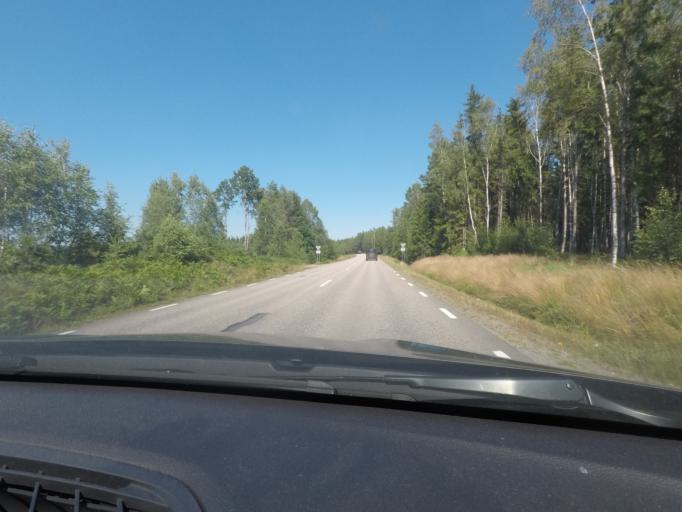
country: SE
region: Kronoberg
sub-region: Markaryds Kommun
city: Markaryd
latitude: 56.4750
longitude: 13.5269
